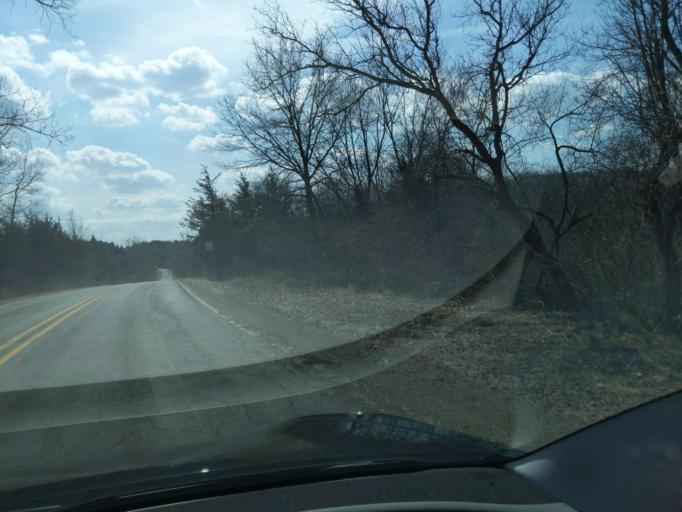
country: US
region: Michigan
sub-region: Washtenaw County
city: Chelsea
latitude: 42.4029
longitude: -84.0403
